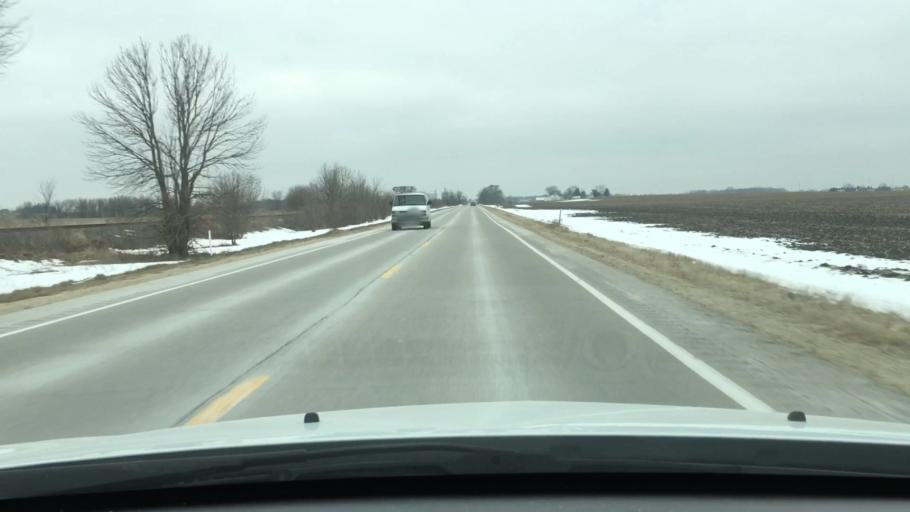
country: US
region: Illinois
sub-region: DeKalb County
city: Waterman
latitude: 41.7695
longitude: -88.7210
